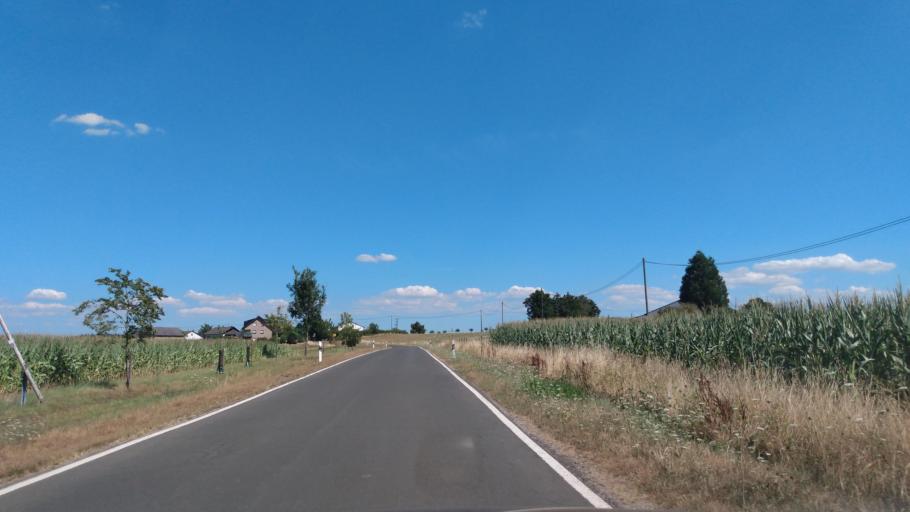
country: DE
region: Rheinland-Pfalz
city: Landscheid
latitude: 49.9959
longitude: 6.7826
